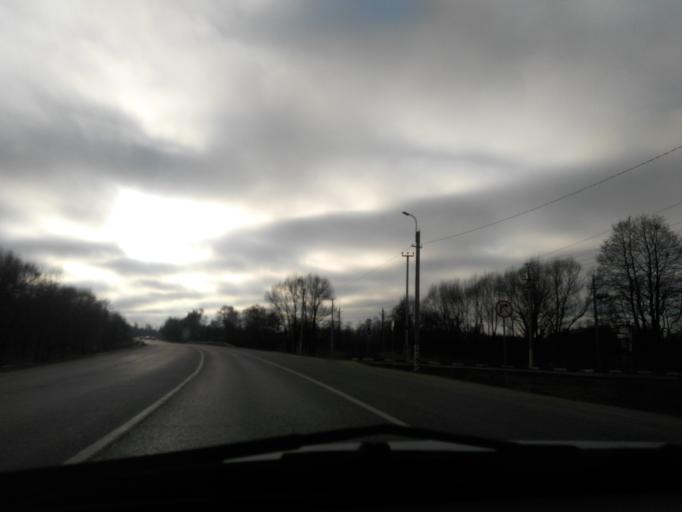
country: RU
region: Moskovskaya
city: Troitsk
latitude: 55.3429
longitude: 37.1732
